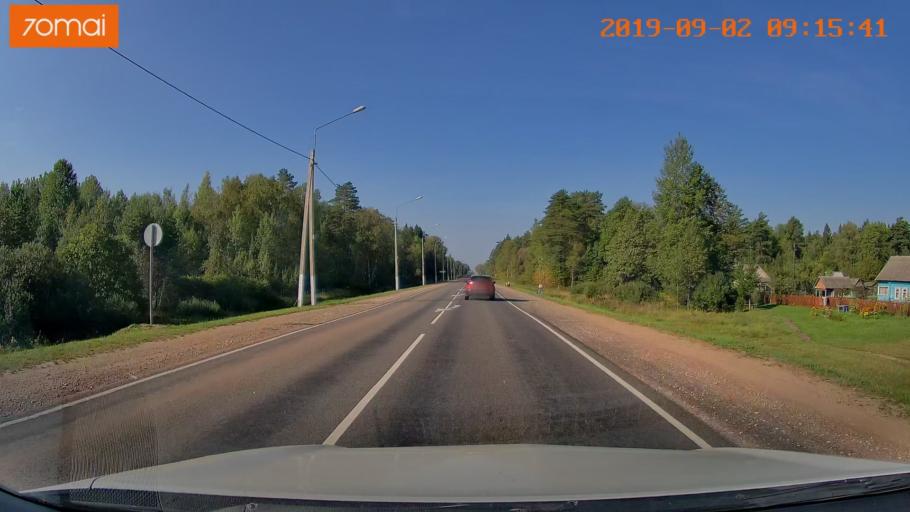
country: RU
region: Kaluga
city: Nikola-Lenivets
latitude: 54.8374
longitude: 35.4893
